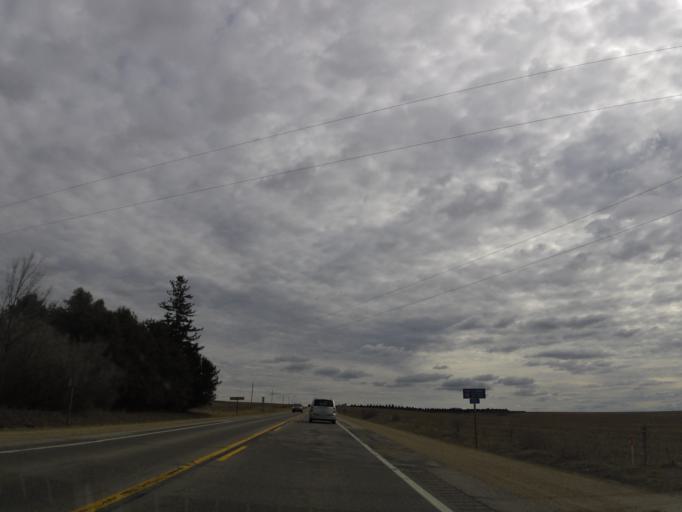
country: US
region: Iowa
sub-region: Chickasaw County
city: New Hampton
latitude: 43.1986
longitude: -92.2983
